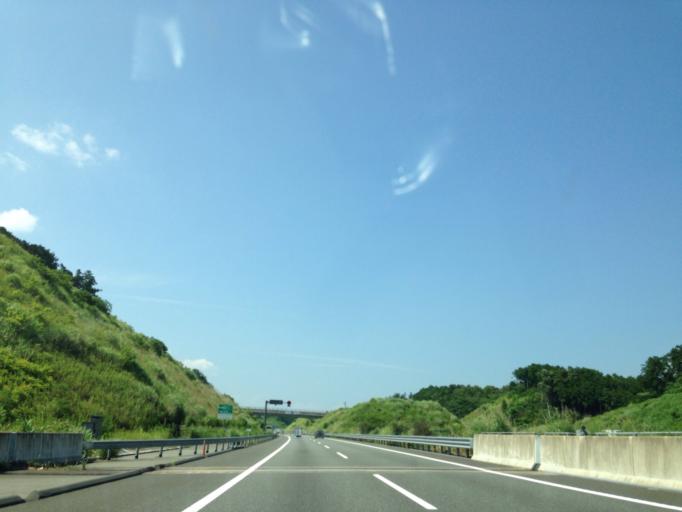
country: JP
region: Shizuoka
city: Mishima
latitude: 35.1859
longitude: 138.8881
